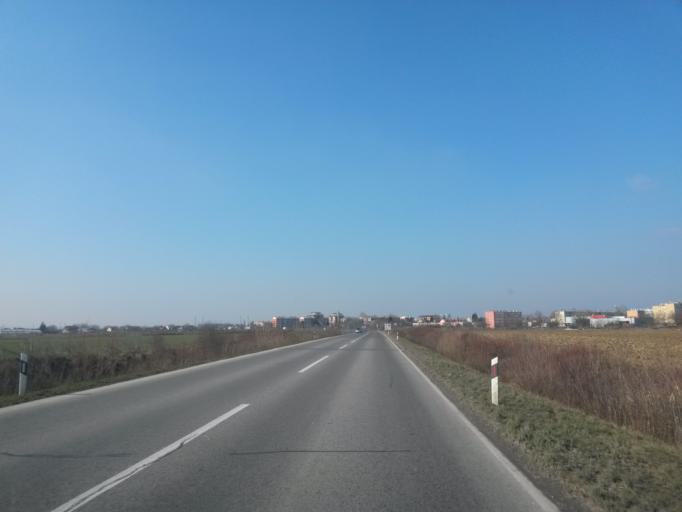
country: HR
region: Osjecko-Baranjska
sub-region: Grad Osijek
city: Osijek
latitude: 45.5394
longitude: 18.7232
